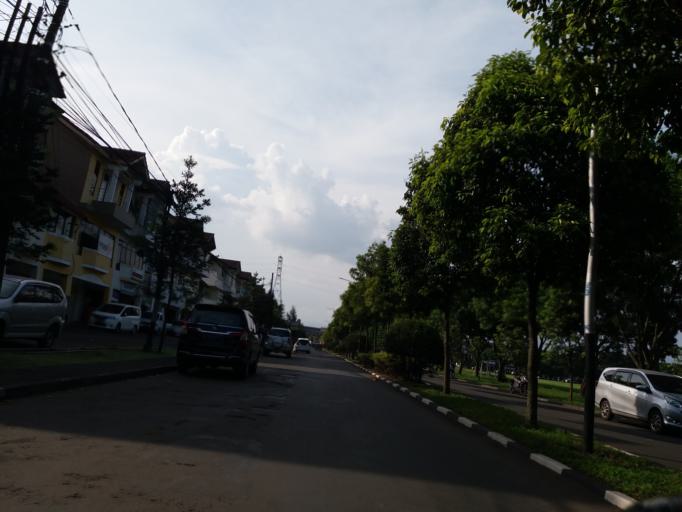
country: ID
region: West Java
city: Bandung
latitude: -6.9559
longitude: 107.6270
